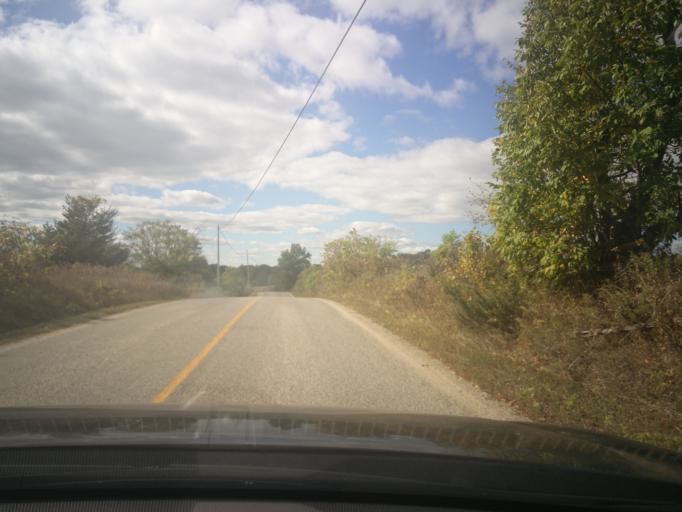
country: CA
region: Ontario
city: Perth
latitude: 44.6582
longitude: -76.5708
